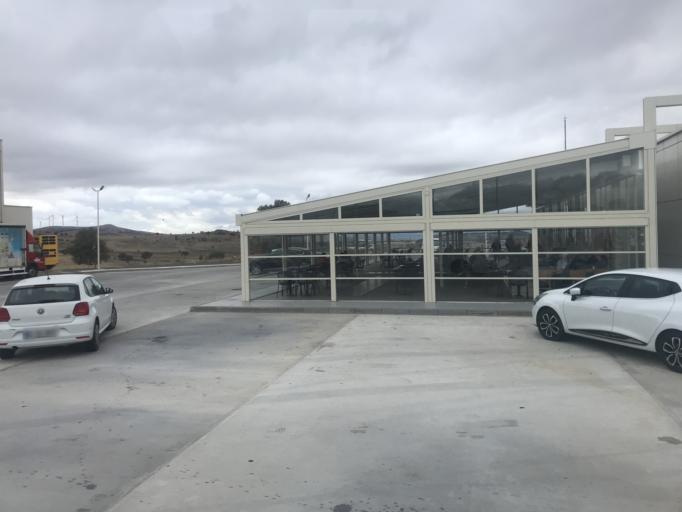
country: TR
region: Balikesir
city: Yenikoy
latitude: 39.7563
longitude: 27.9636
